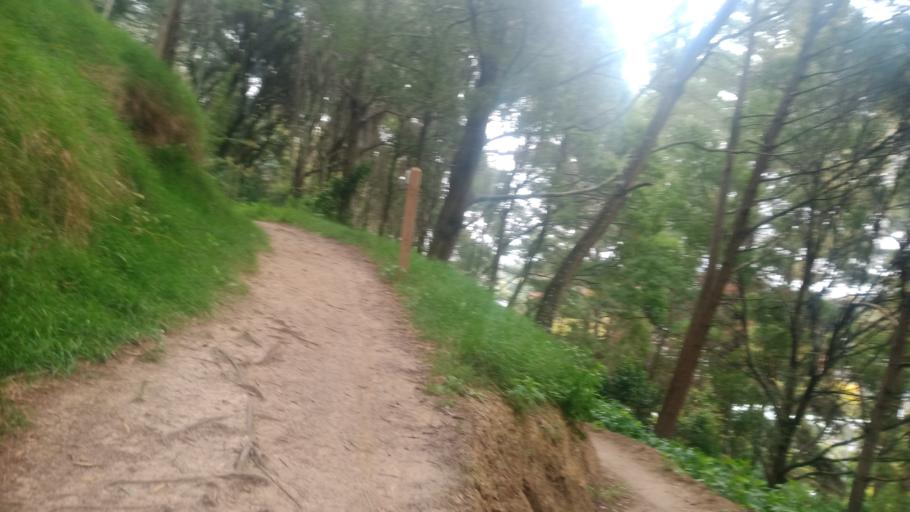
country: NZ
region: Gisborne
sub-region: Gisborne District
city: Gisborne
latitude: -38.6552
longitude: 178.0417
